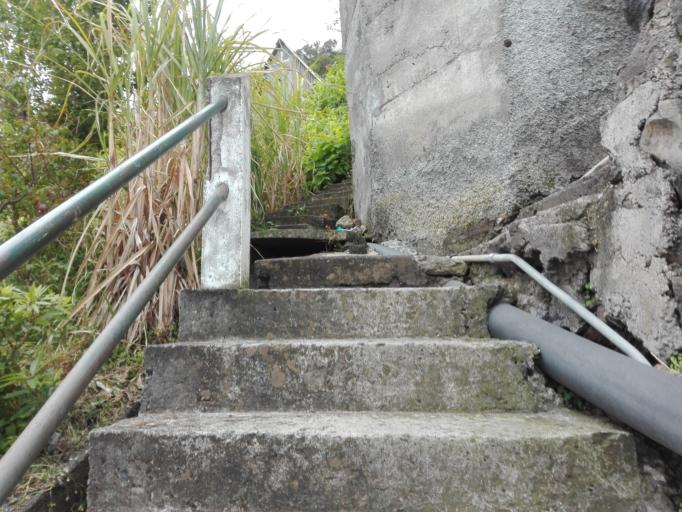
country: PT
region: Madeira
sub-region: Santana
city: Santana
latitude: 32.7734
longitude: -16.8326
